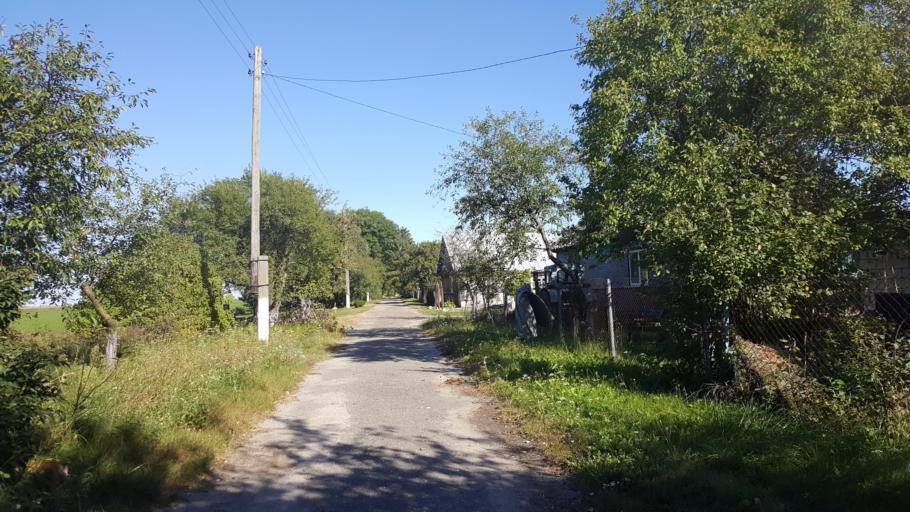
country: PL
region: Lublin Voivodeship
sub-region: Powiat bialski
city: Janow Podlaski
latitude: 52.2401
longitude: 23.2395
